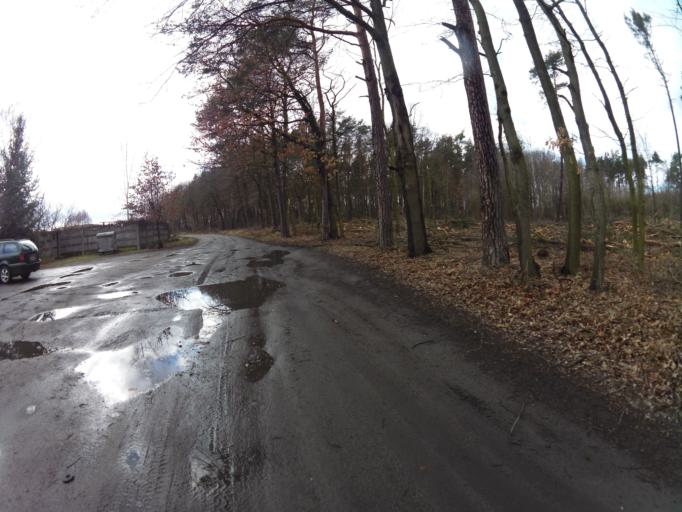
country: PL
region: West Pomeranian Voivodeship
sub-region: Powiat mysliborski
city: Debno
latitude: 52.7344
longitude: 14.7205
